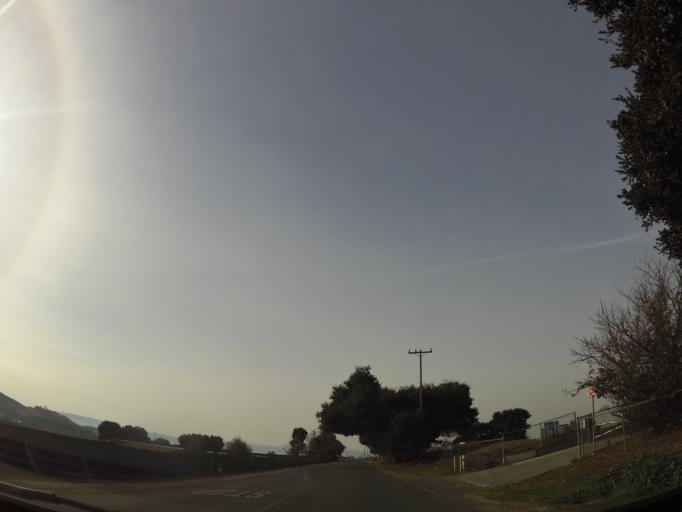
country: US
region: California
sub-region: Monterey County
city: Prunedale
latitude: 36.7725
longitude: -121.6046
